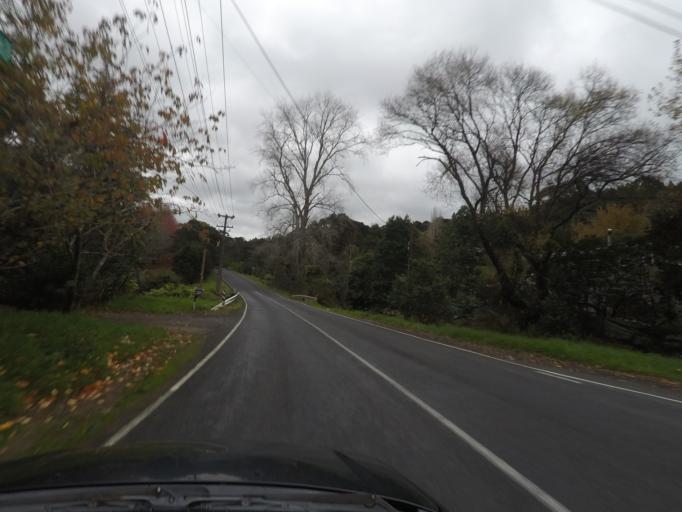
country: NZ
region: Auckland
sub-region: Auckland
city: Waitakere
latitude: -36.9186
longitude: 174.6077
